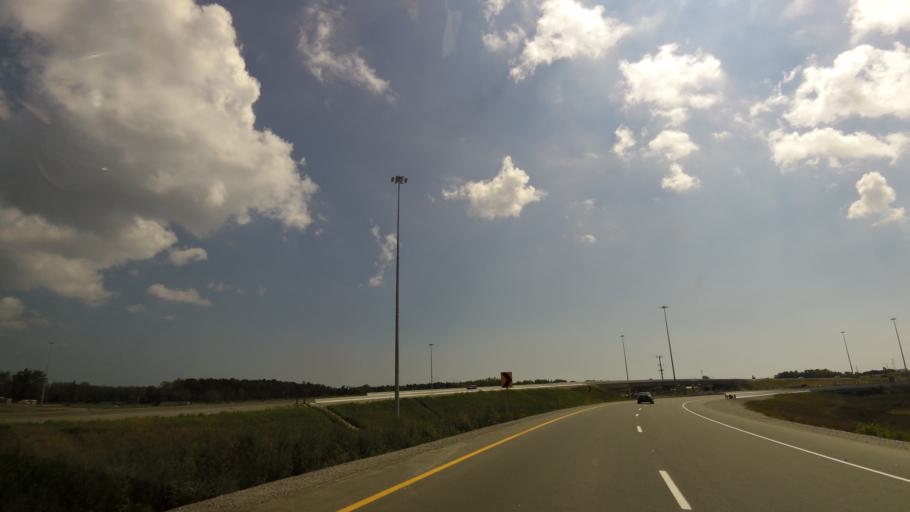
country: CA
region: Ontario
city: Ajax
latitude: 43.8673
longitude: -78.9756
